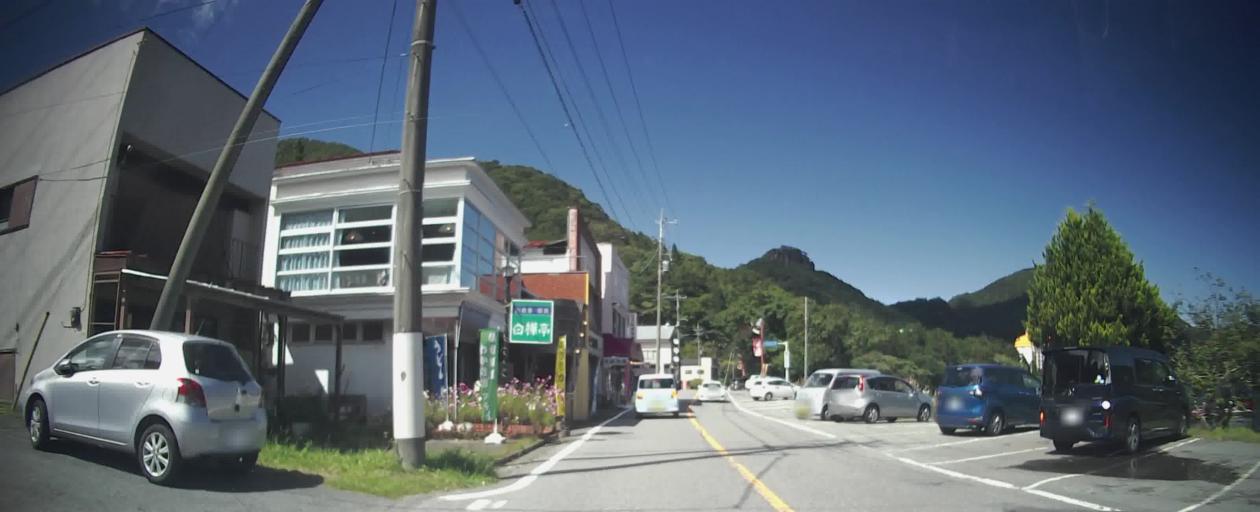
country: JP
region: Gunma
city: Nakanojomachi
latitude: 36.4715
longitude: 138.8608
